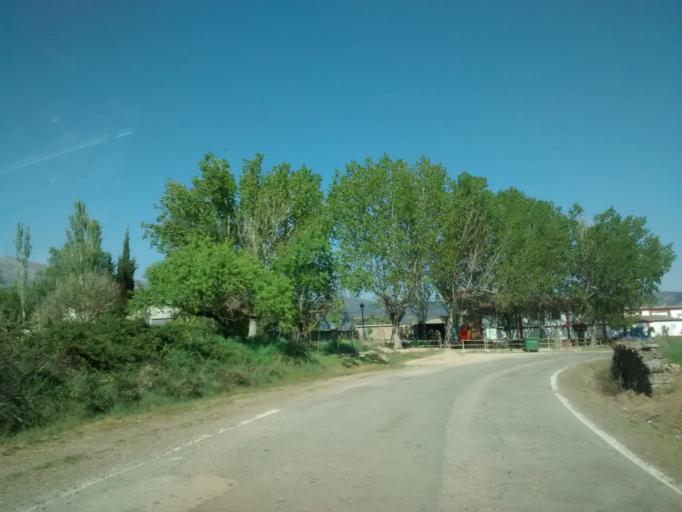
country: ES
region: Aragon
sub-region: Provincia de Huesca
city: Ibieca
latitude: 42.2035
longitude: -0.2090
